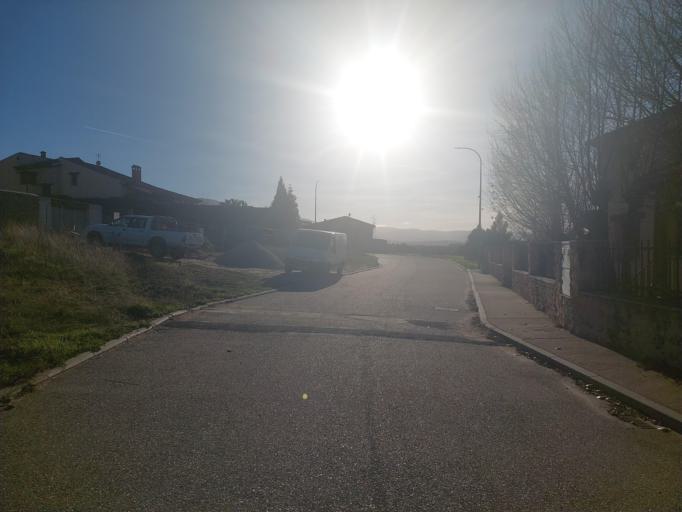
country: ES
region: Castille and Leon
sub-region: Provincia de Segovia
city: Pradena
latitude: 41.1363
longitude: -3.6932
